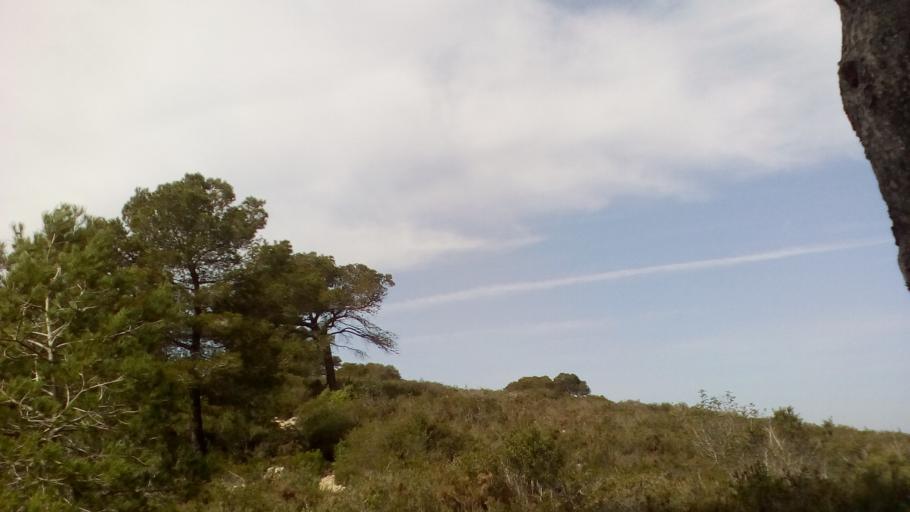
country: ES
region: Valencia
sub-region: Provincia de Valencia
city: Xeraco,Jaraco
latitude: 39.0389
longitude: -0.2464
